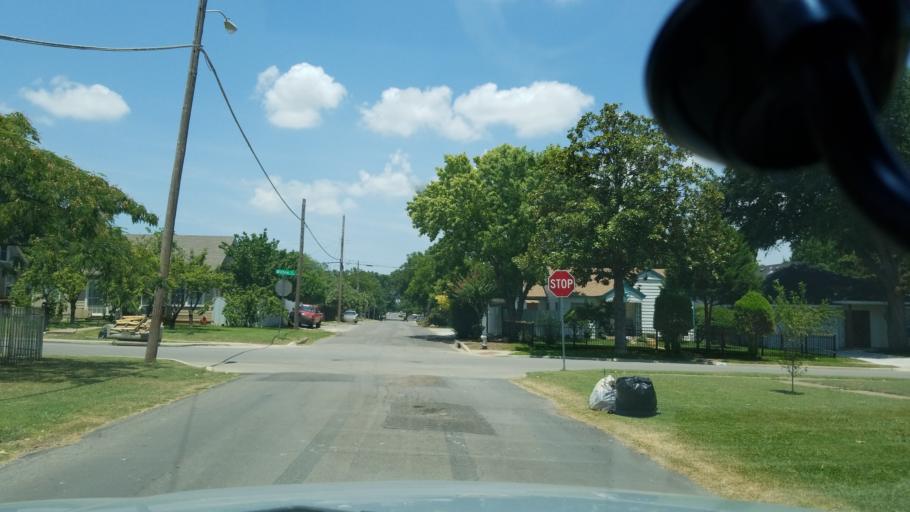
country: US
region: Texas
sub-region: Dallas County
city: Cockrell Hill
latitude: 32.7290
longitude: -96.8592
